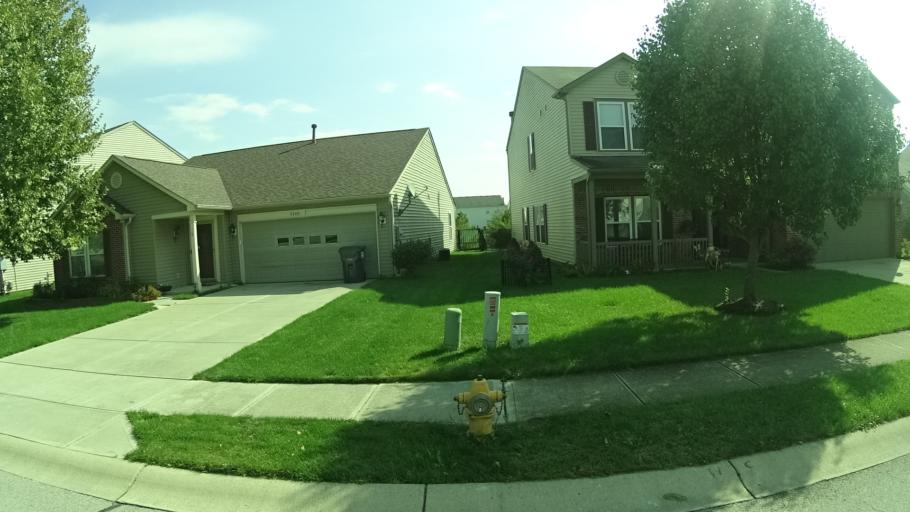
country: US
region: Indiana
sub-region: Hancock County
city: Fortville
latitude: 39.9834
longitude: -85.8560
